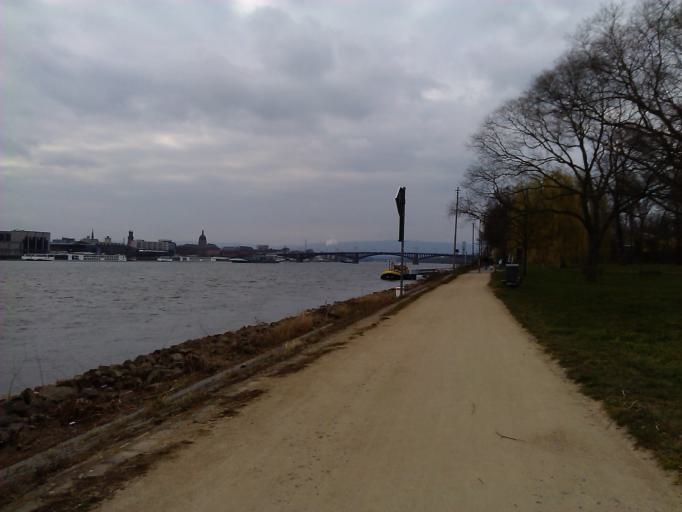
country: DE
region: Rheinland-Pfalz
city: Mainz
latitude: 49.9988
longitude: 8.2880
